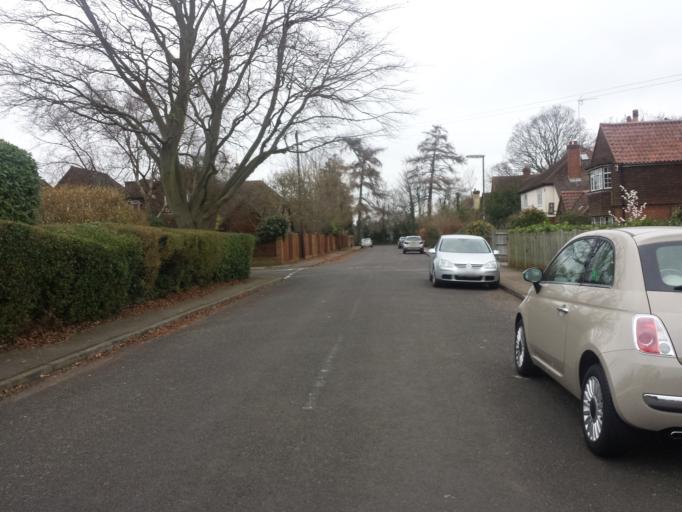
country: GB
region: England
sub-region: Surrey
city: Godalming
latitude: 51.1801
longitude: -0.6095
